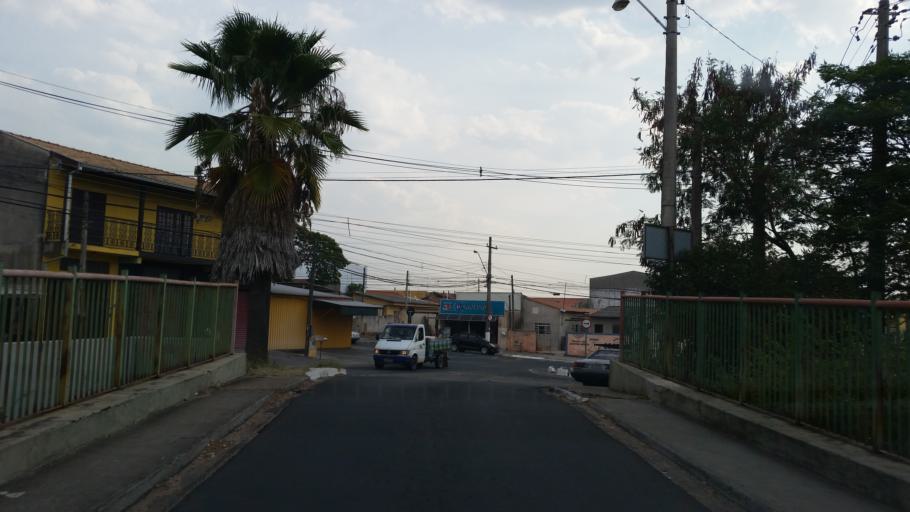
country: BR
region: Sao Paulo
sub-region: Hortolandia
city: Hortolandia
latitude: -22.8891
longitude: -47.1792
